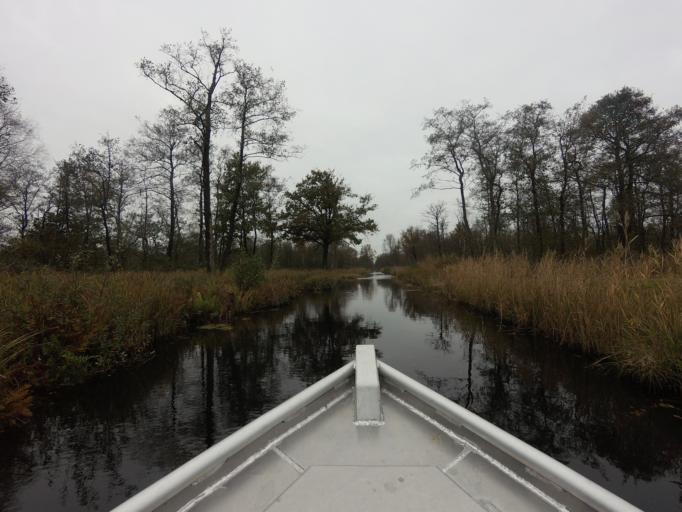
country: NL
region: Overijssel
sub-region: Gemeente Steenwijkerland
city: Oldemarkt
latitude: 52.7868
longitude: 5.9495
